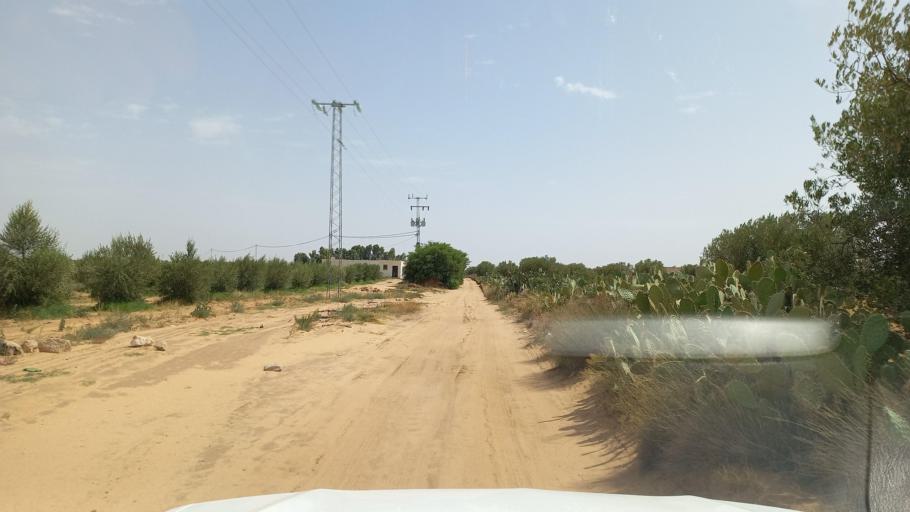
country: TN
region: Al Qasrayn
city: Kasserine
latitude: 35.2587
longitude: 9.0531
